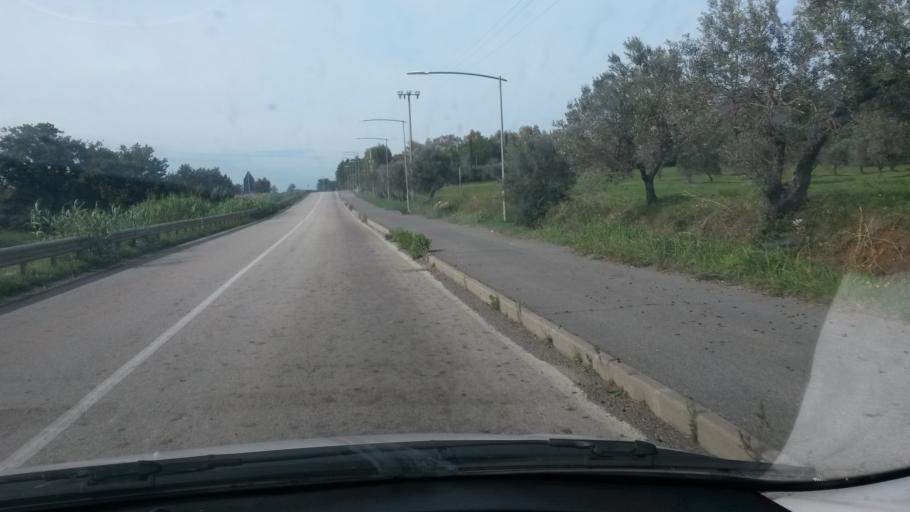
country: IT
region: Tuscany
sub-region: Provincia di Livorno
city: S.P. in Palazzi
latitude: 43.3336
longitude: 10.5214
